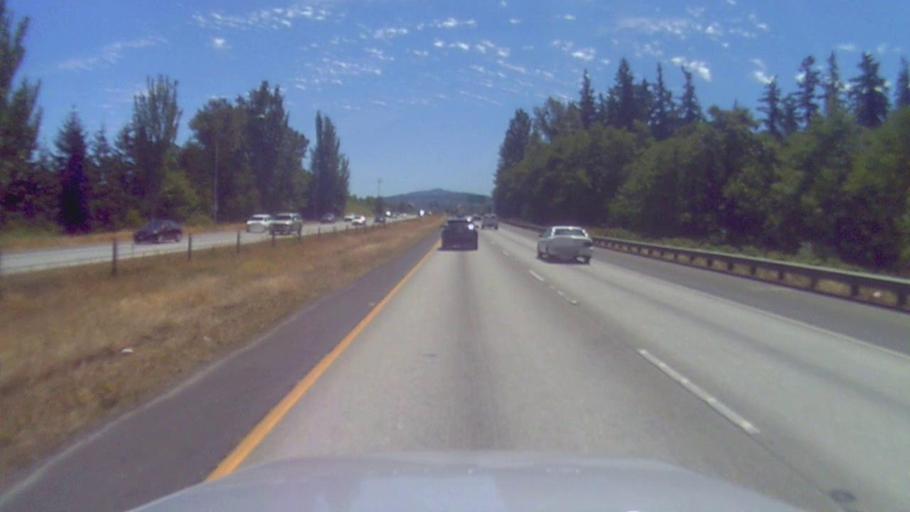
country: US
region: Washington
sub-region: Whatcom County
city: Bellingham
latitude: 48.7755
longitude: -122.4680
